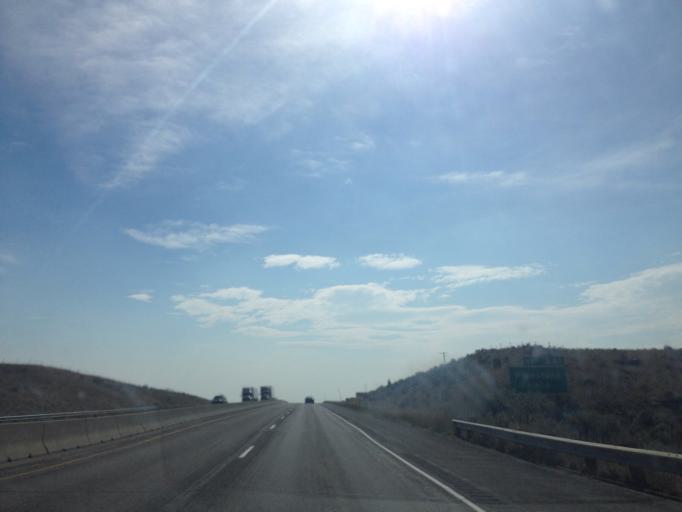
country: US
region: Montana
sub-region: Jefferson County
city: Whitehall
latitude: 45.9117
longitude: -112.2668
